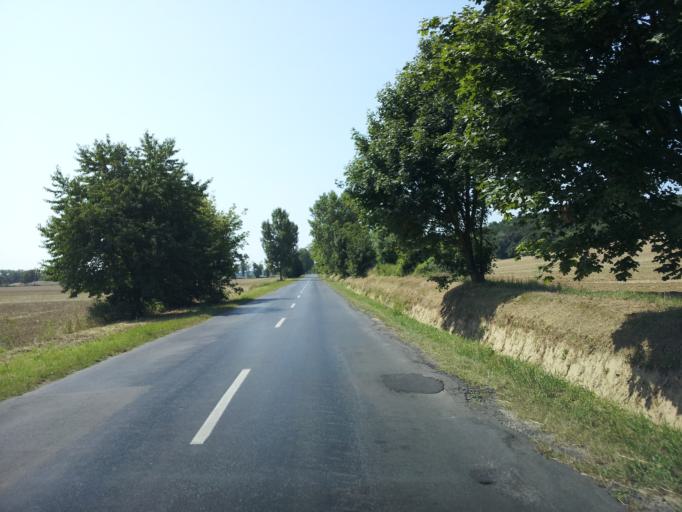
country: HU
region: Zala
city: Heviz
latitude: 46.8336
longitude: 17.0926
